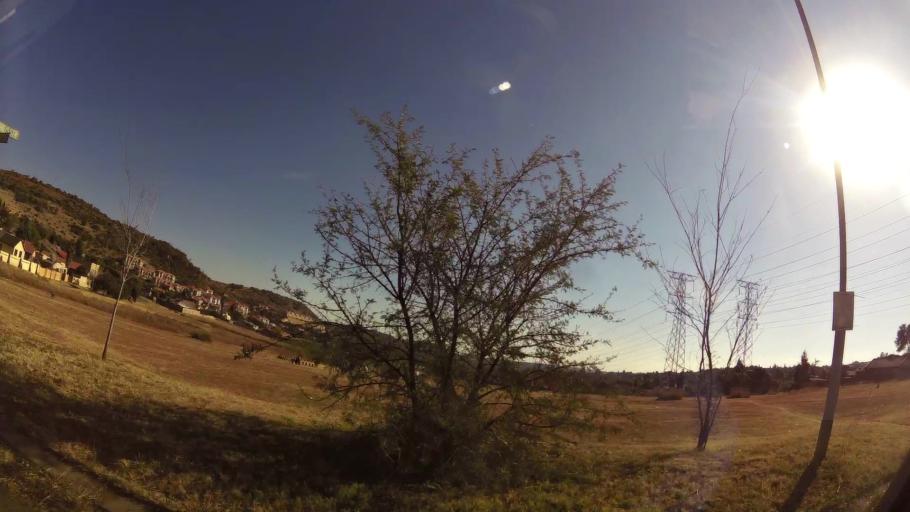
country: ZA
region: Gauteng
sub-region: City of Johannesburg Metropolitan Municipality
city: Johannesburg
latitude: -26.2762
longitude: 28.0273
